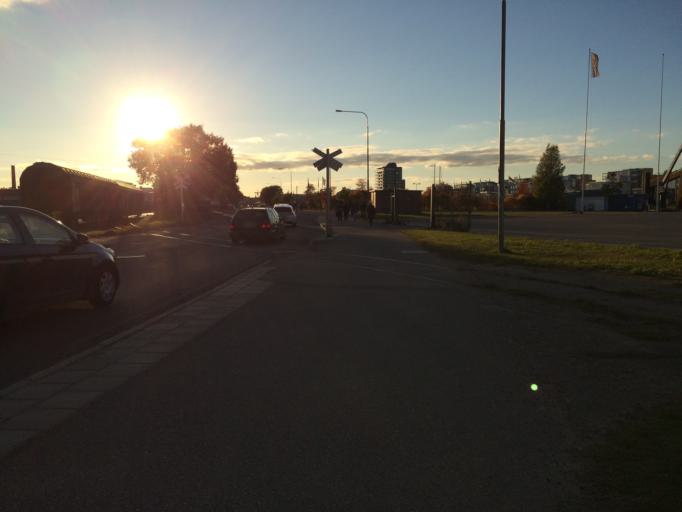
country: SE
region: Gaevleborg
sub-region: Gavle Kommun
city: Gavle
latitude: 60.6784
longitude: 17.1732
